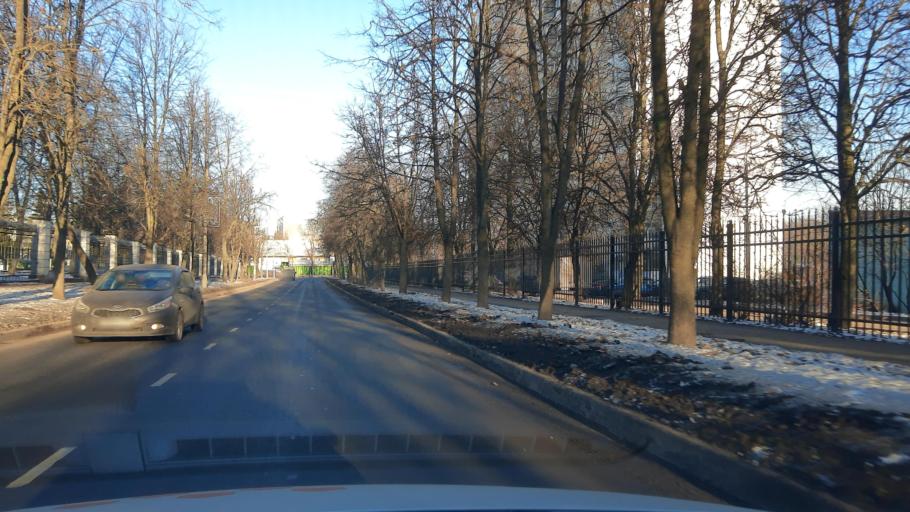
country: RU
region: Moskovskaya
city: Mosrentgen
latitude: 55.6137
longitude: 37.4701
